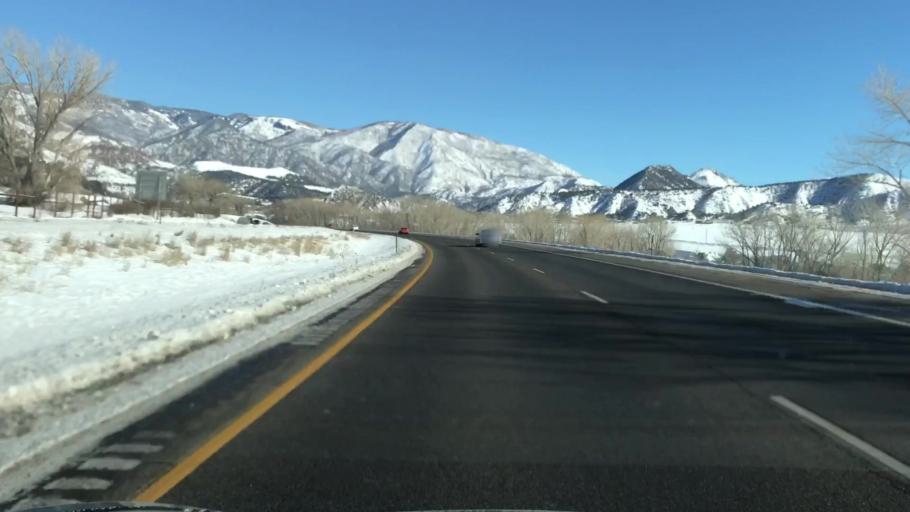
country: US
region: Colorado
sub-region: Garfield County
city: New Castle
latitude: 39.5656
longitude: -107.4919
